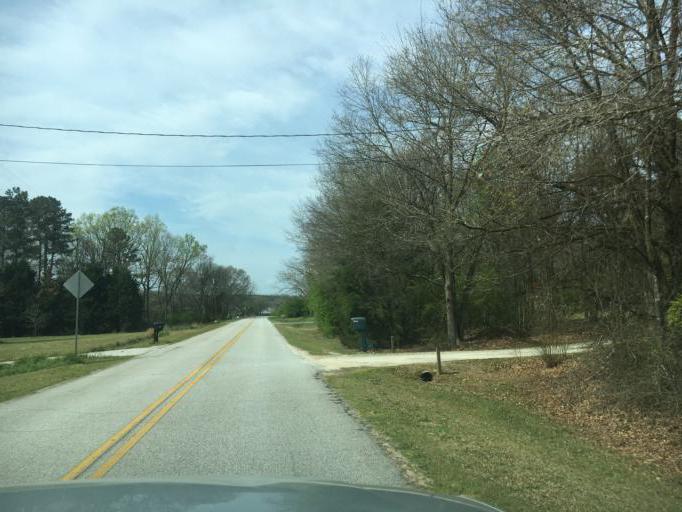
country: US
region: Georgia
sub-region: Franklin County
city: Lavonia
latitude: 34.4386
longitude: -83.0360
